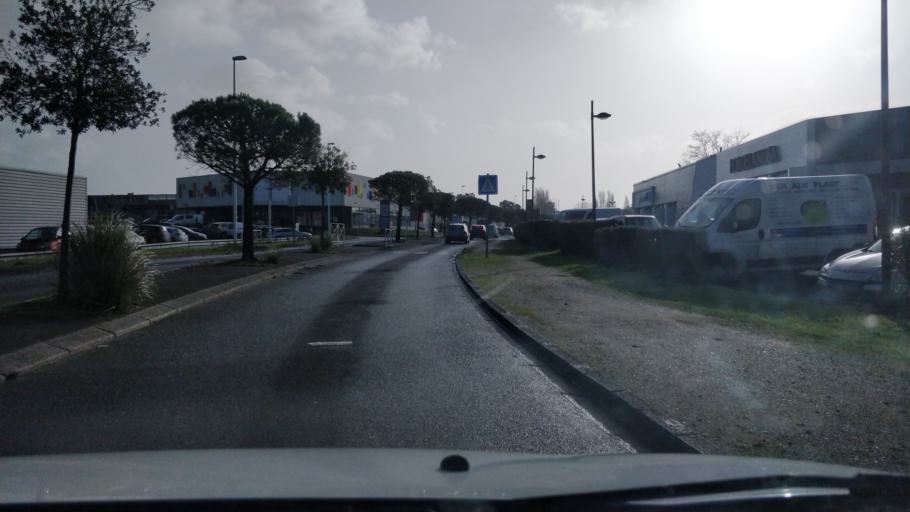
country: FR
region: Pays de la Loire
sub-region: Departement de la Loire-Atlantique
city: La Baule-Escoublac
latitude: 47.2940
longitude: -2.3976
